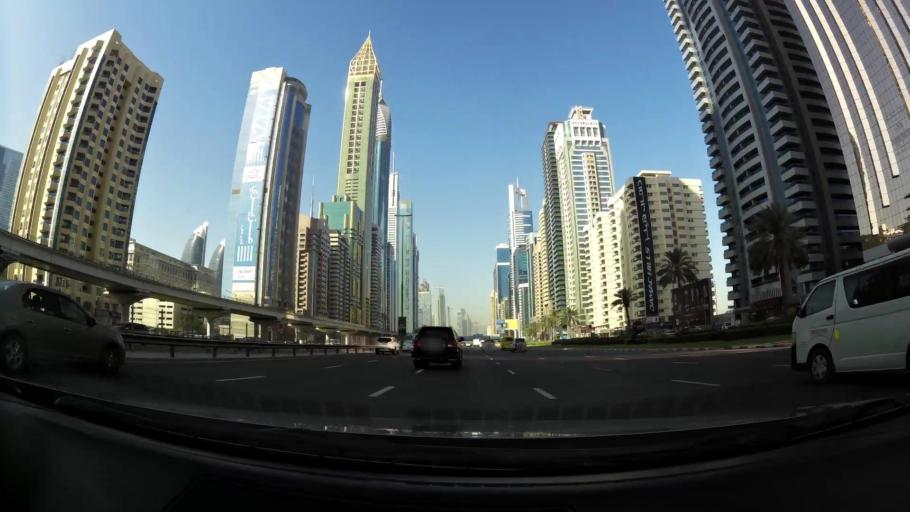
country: AE
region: Ash Shariqah
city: Sharjah
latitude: 25.2161
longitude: 55.2783
